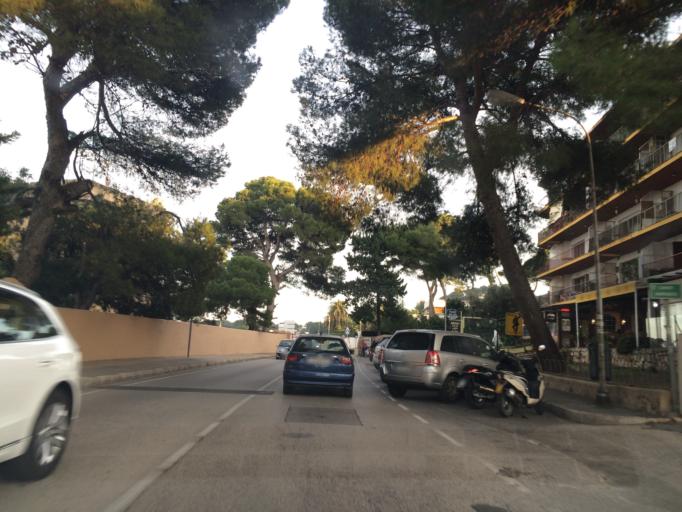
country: ES
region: Valencia
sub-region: Provincia de Alicante
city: Denia
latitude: 38.8345
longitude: 0.1214
